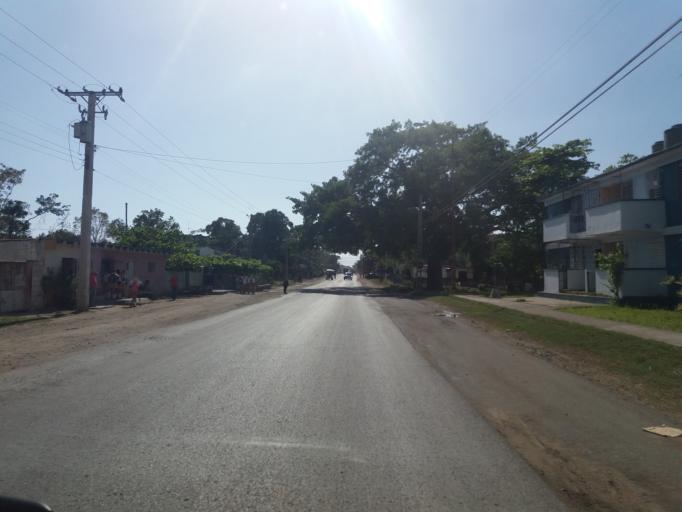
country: CU
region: Cienfuegos
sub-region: Municipio de Cienfuegos
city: Cienfuegos
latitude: 22.1572
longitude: -80.4294
